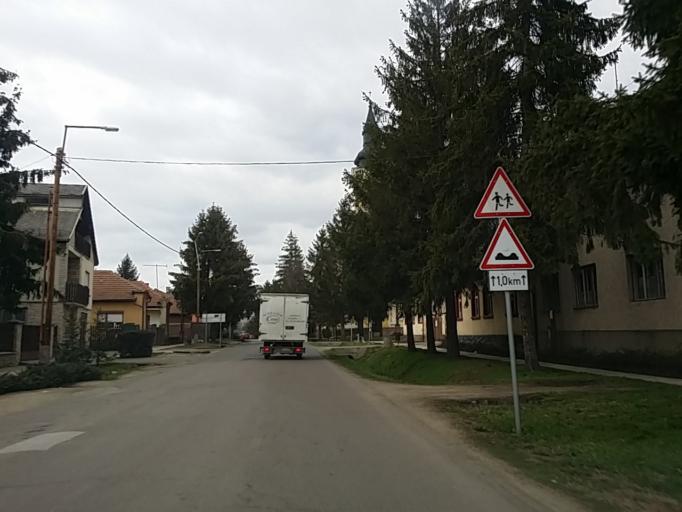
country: HU
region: Heves
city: Kompolt
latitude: 47.7593
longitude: 20.2472
